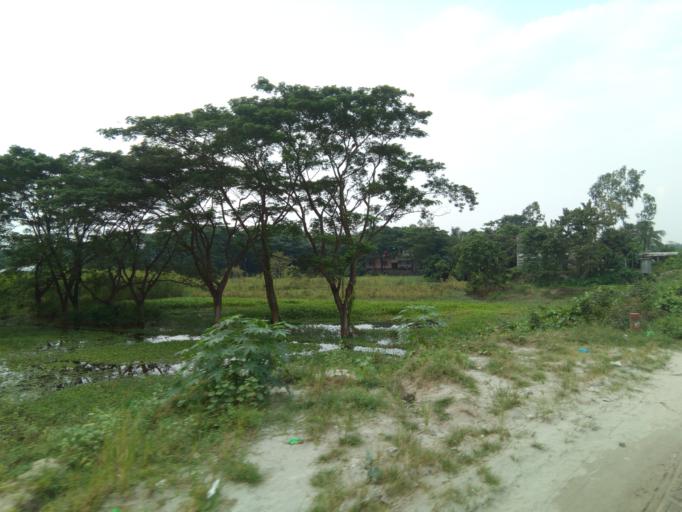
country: BD
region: Dhaka
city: Dohar
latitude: 23.5489
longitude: 90.2998
